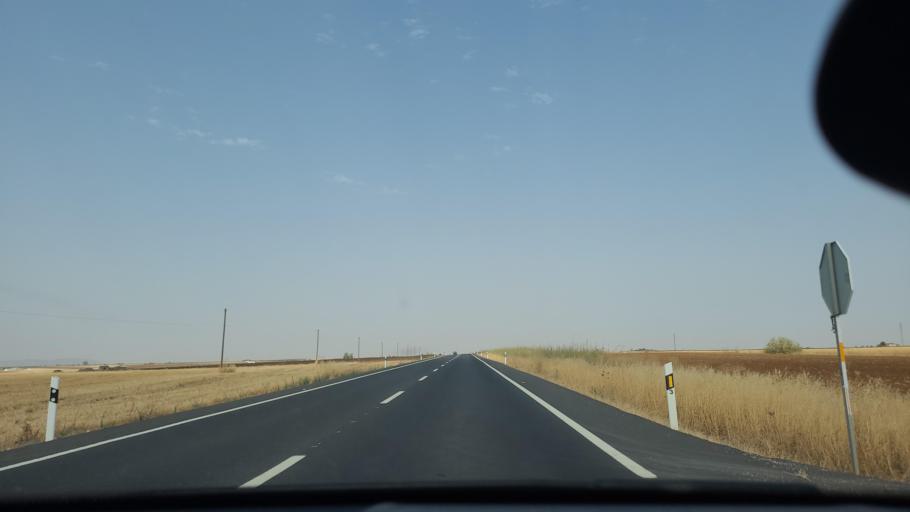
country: ES
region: Extremadura
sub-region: Provincia de Badajoz
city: Azuaga
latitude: 38.2633
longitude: -5.7356
